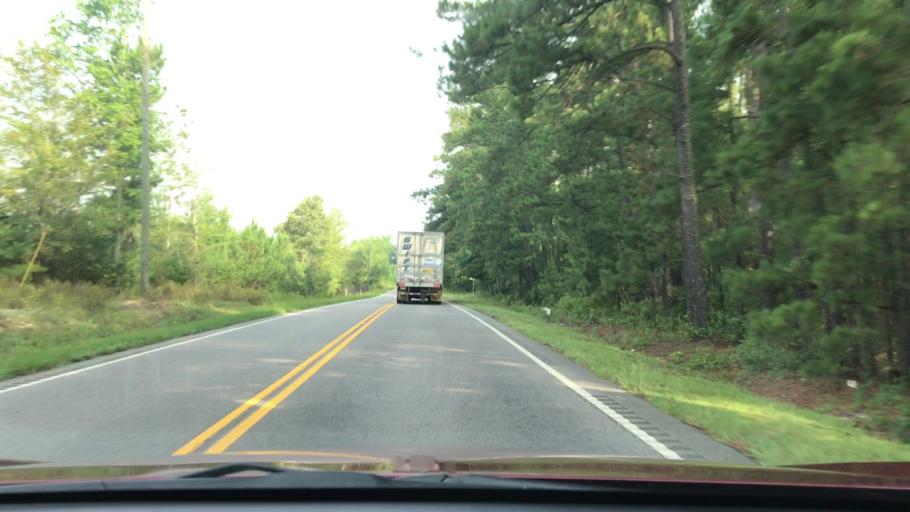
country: US
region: South Carolina
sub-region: Barnwell County
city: Williston
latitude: 33.6212
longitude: -81.2917
